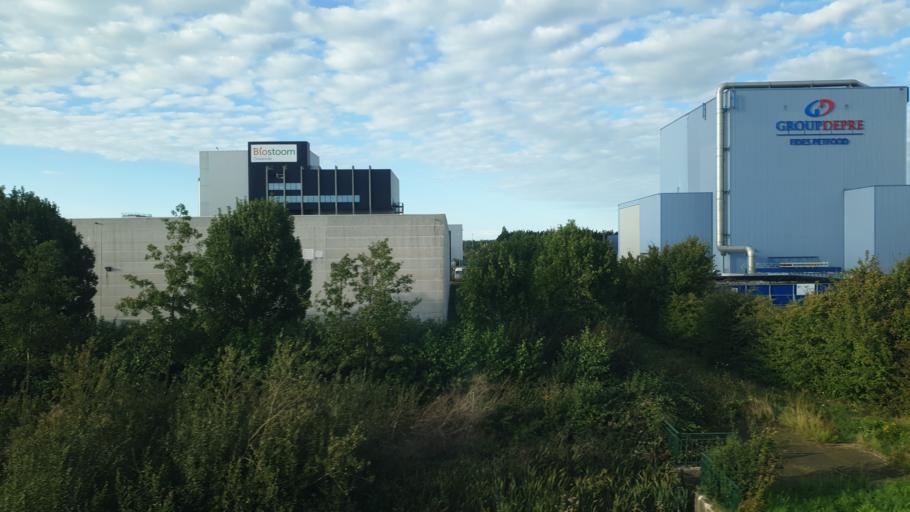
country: BE
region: Flanders
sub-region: Provincie West-Vlaanderen
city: Oudenburg
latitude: 51.2078
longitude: 2.9949
